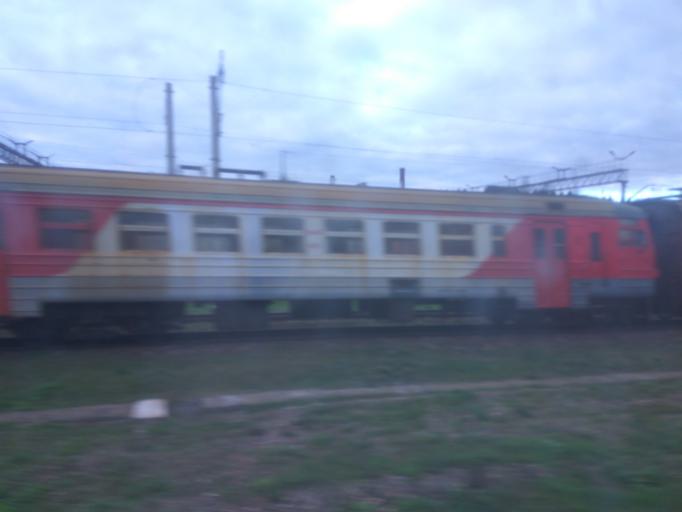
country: RU
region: Moskovskaya
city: Aprelevka
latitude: 55.5580
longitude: 37.0857
